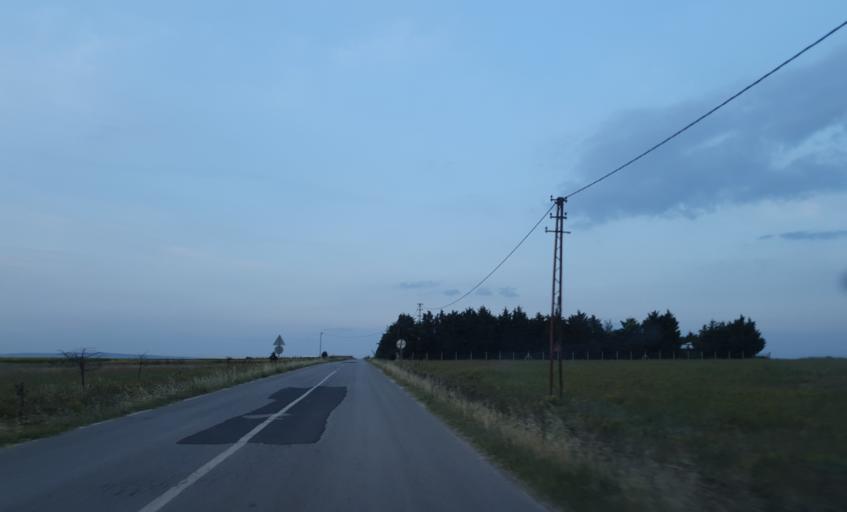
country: TR
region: Tekirdag
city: Beyazkoy
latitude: 41.4149
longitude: 27.6588
